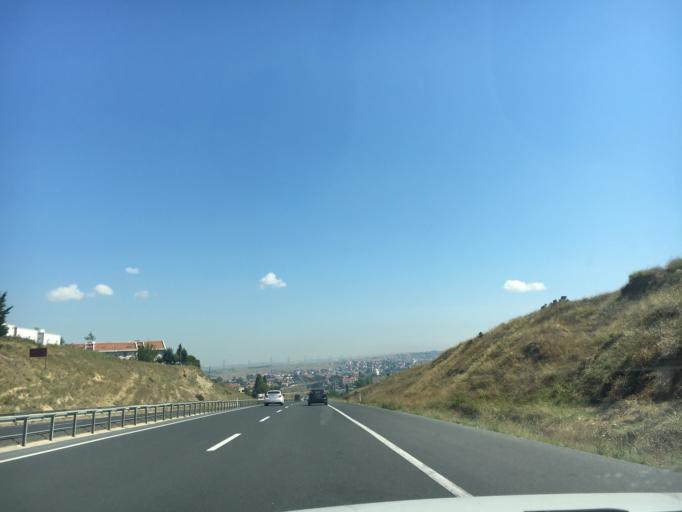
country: TR
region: Tekirdag
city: Sultankoy
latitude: 41.0011
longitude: 27.9759
